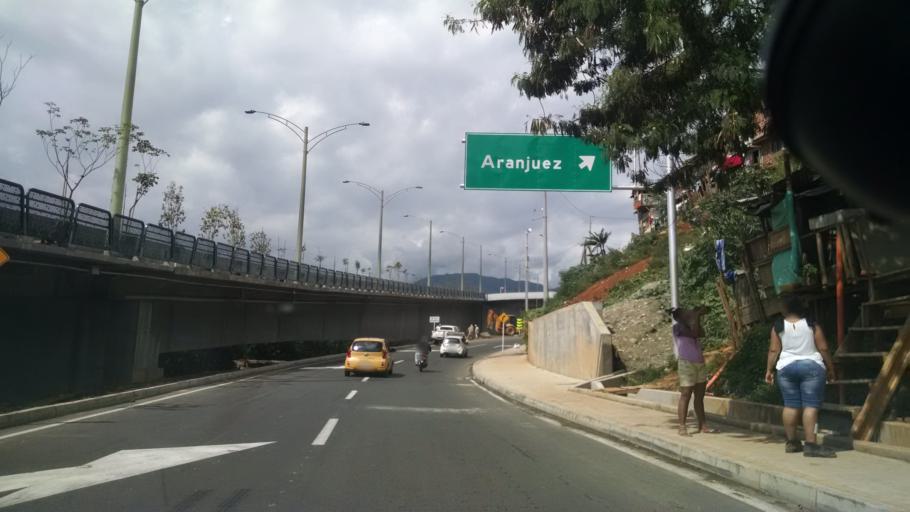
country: CO
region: Antioquia
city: Medellin
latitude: 6.2827
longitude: -75.5679
